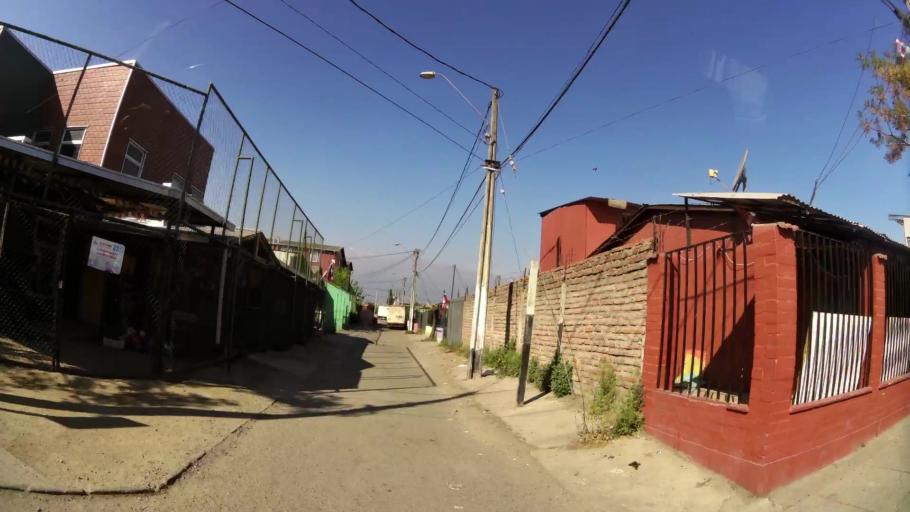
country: CL
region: Santiago Metropolitan
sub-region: Provincia de Santiago
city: La Pintana
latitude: -33.5591
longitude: -70.6169
